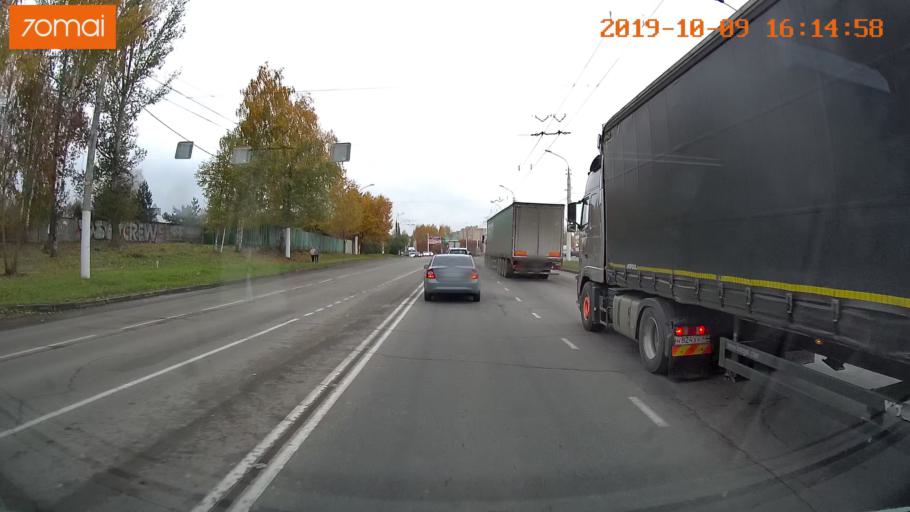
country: RU
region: Kostroma
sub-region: Kostromskoy Rayon
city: Kostroma
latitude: 57.7423
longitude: 40.9206
